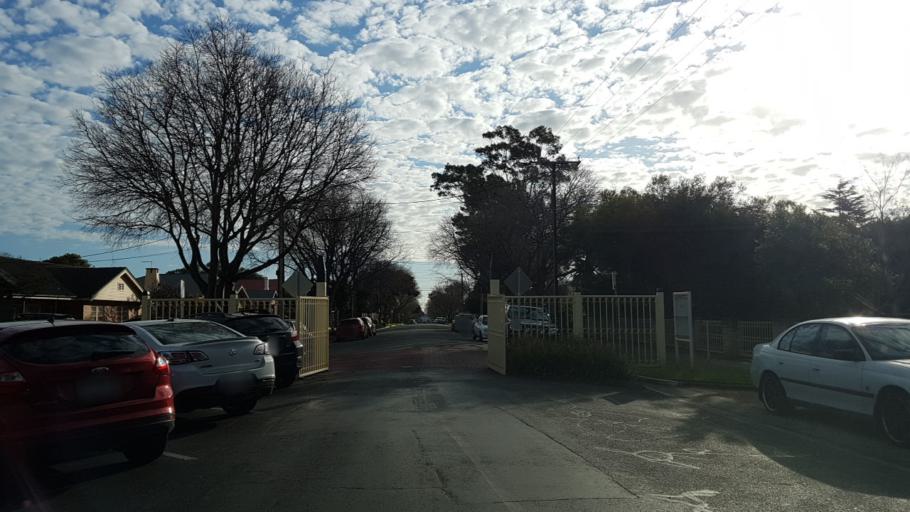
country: AU
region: South Australia
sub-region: Prospect
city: Prospect
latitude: -34.8861
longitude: 138.5988
